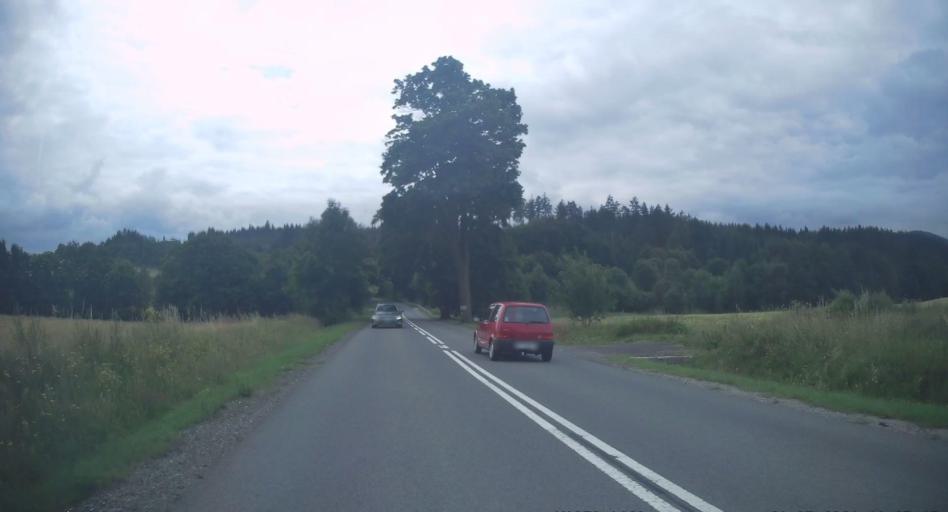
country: PL
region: Lower Silesian Voivodeship
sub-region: Powiat walbrzyski
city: Dziecmorowice
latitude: 50.7469
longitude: 16.3352
